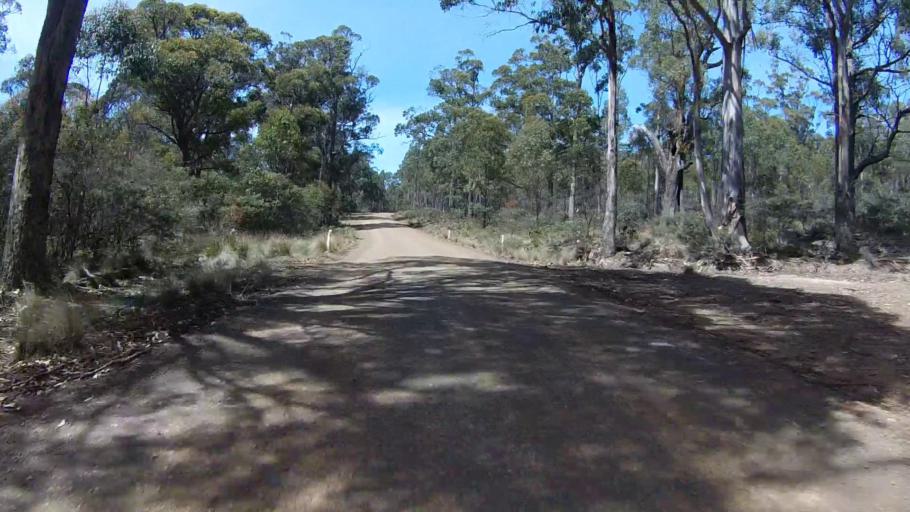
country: AU
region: Tasmania
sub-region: Sorell
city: Sorell
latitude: -42.6674
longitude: 147.7302
